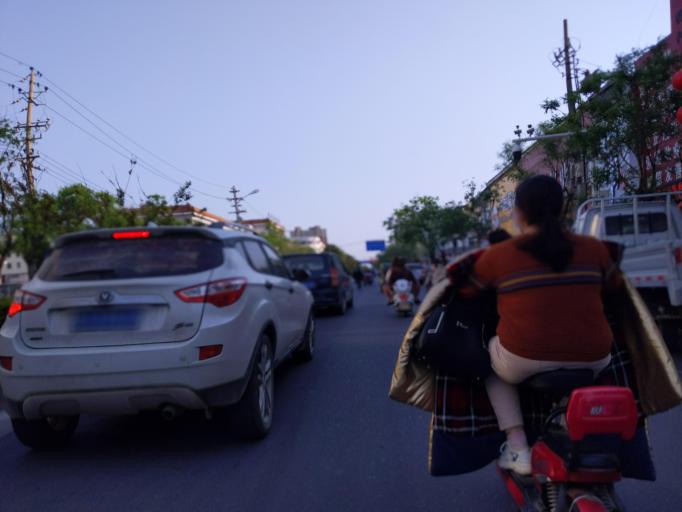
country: CN
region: Henan Sheng
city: Puyang Chengguanzhen
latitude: 35.7030
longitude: 115.0163
